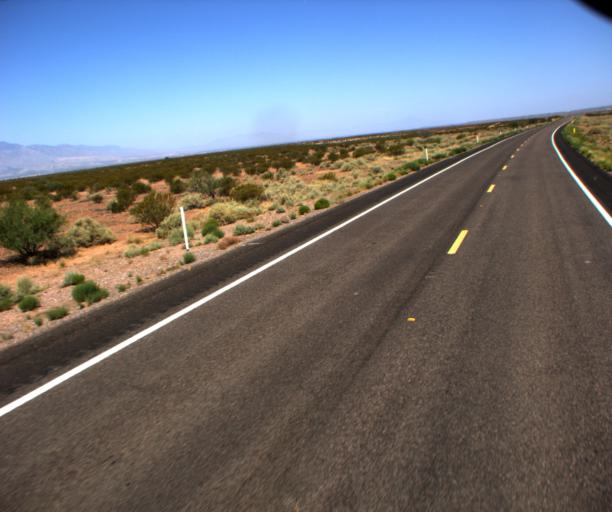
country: US
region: Arizona
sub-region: Graham County
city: Safford
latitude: 32.7848
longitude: -109.5406
